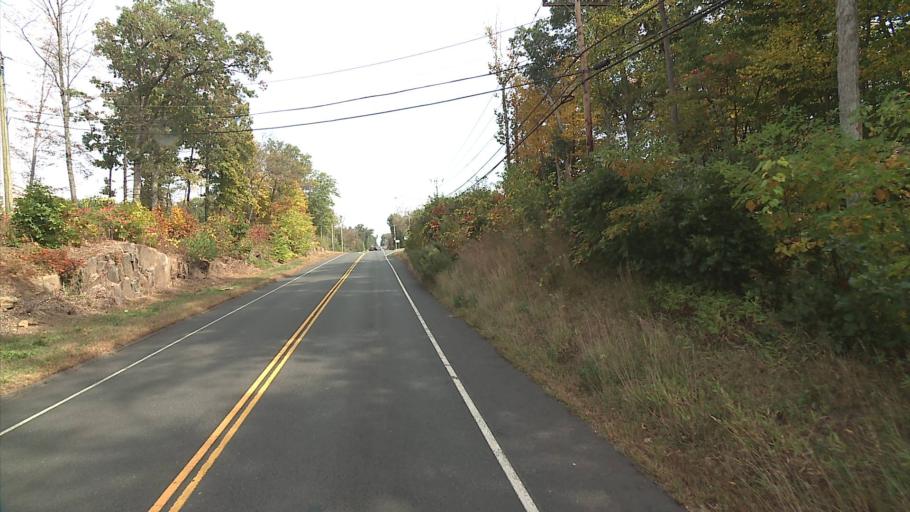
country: US
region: Connecticut
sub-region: Hartford County
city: Farmington
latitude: 41.7070
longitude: -72.8167
